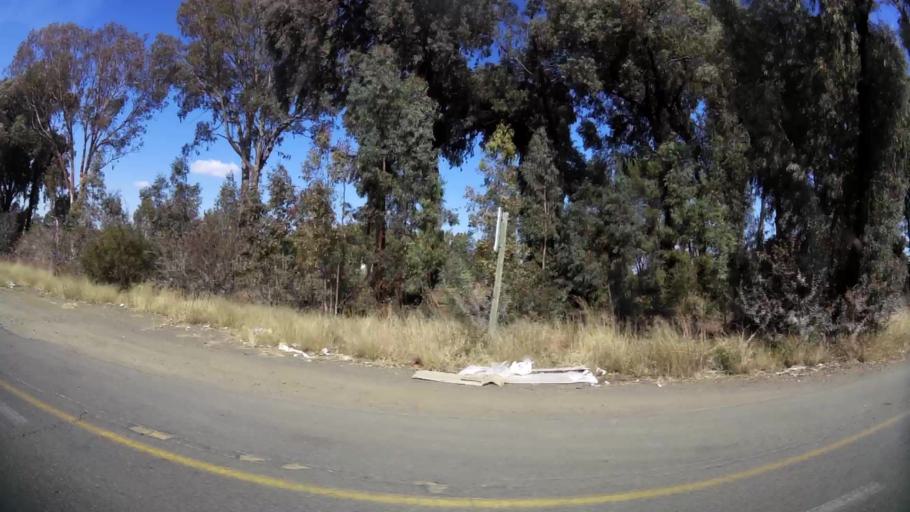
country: ZA
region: Orange Free State
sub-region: Mangaung Metropolitan Municipality
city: Bloemfontein
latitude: -29.1160
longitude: 26.2592
